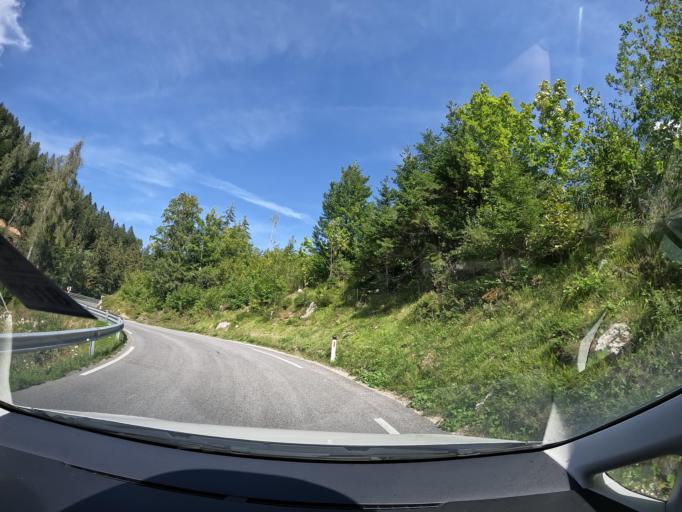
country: AT
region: Carinthia
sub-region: Politischer Bezirk Villach Land
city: Velden am Woerthersee
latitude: 46.5940
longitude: 14.0635
